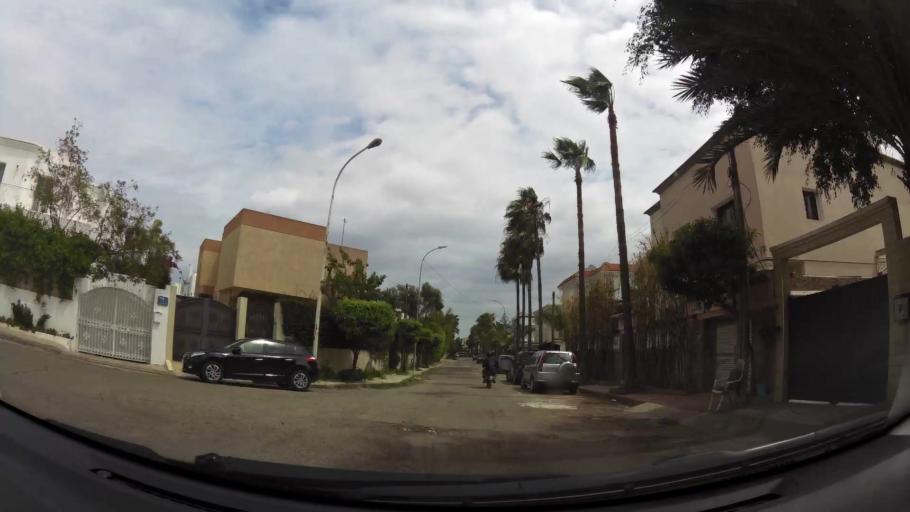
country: MA
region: Grand Casablanca
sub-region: Casablanca
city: Casablanca
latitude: 33.5707
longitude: -7.6645
